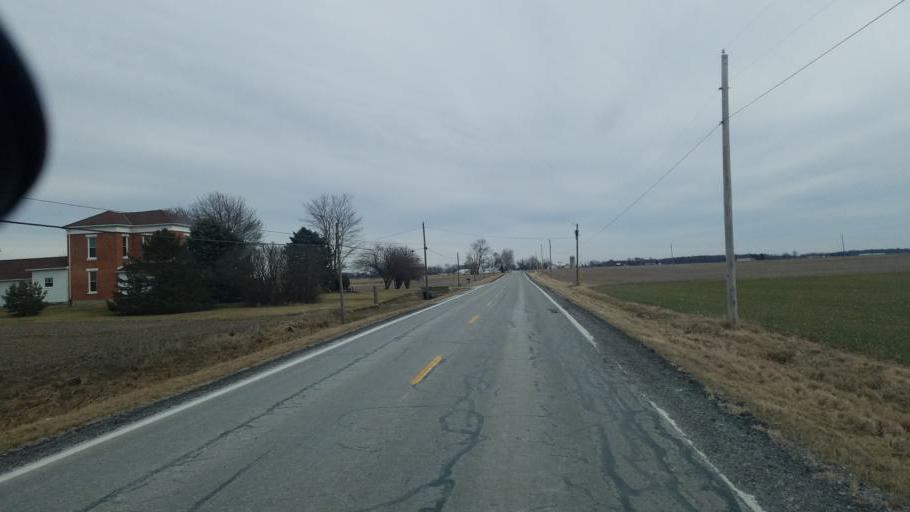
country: US
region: Ohio
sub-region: Marion County
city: Prospect
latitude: 40.4517
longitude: -83.1601
